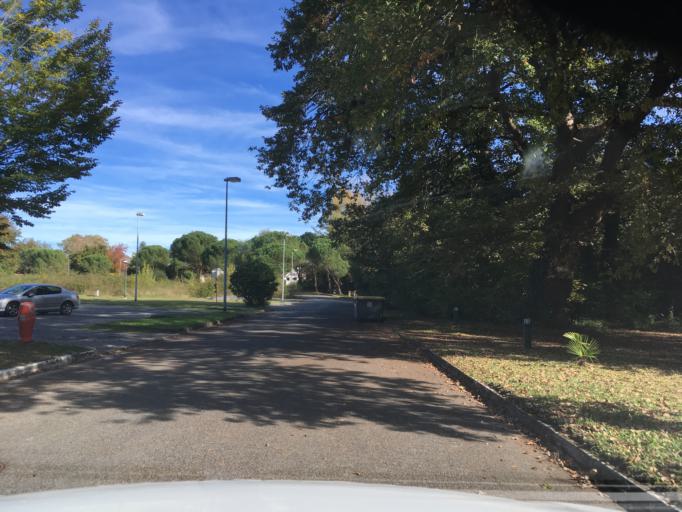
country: FR
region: Aquitaine
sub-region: Departement des Pyrenees-Atlantiques
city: Pau
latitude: 43.3275
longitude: -0.3553
